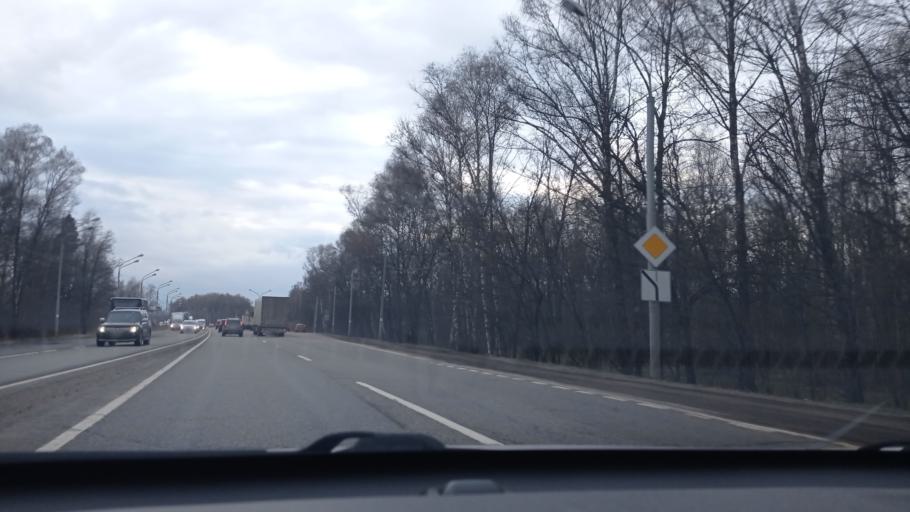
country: RU
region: Moskovskaya
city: Noginsk
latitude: 55.8567
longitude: 38.5276
